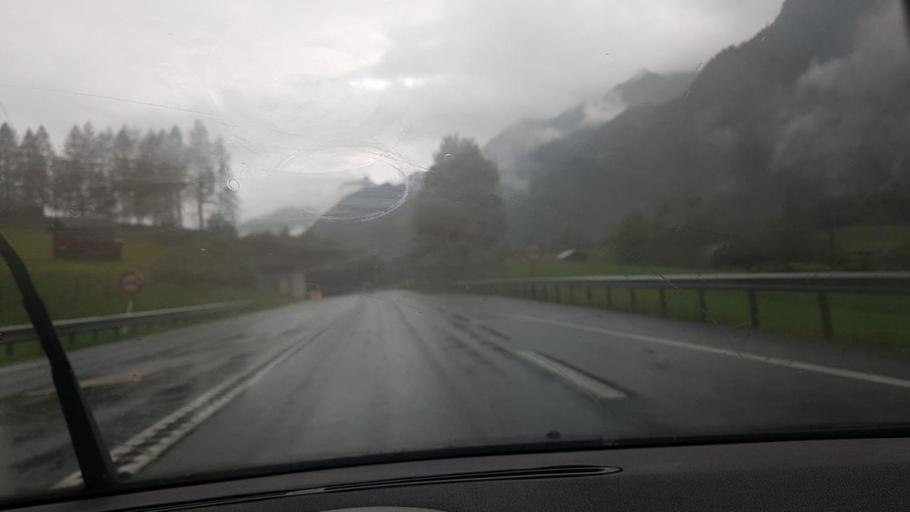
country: AT
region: Tyrol
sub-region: Politischer Bezirk Landeck
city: Flirsch
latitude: 47.1487
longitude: 10.3703
